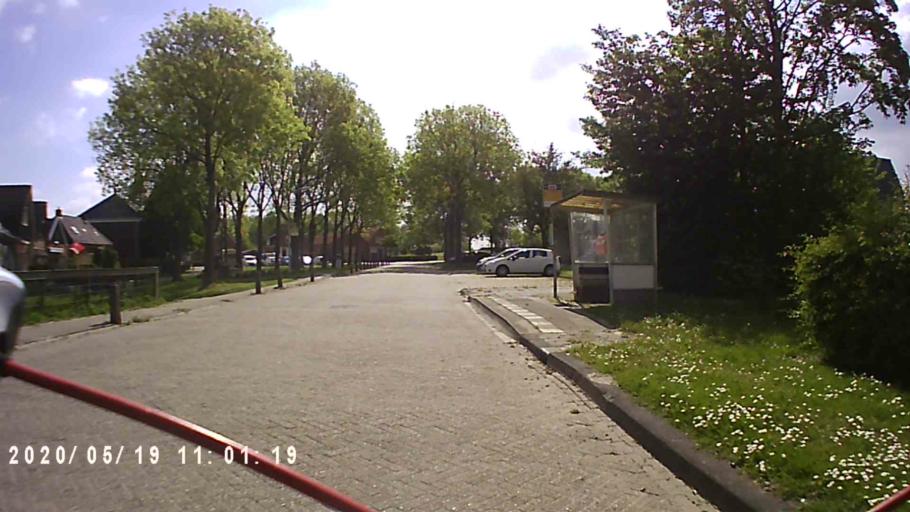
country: NL
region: Groningen
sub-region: Gemeente Zuidhorn
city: Grijpskerk
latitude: 53.3028
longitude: 6.2728
